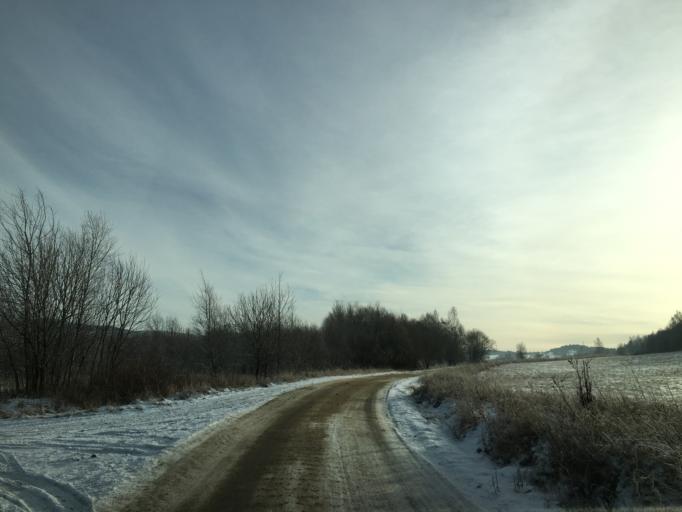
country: PL
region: Lower Silesian Voivodeship
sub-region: Powiat walbrzyski
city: Gluszyca
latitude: 50.6787
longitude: 16.3542
